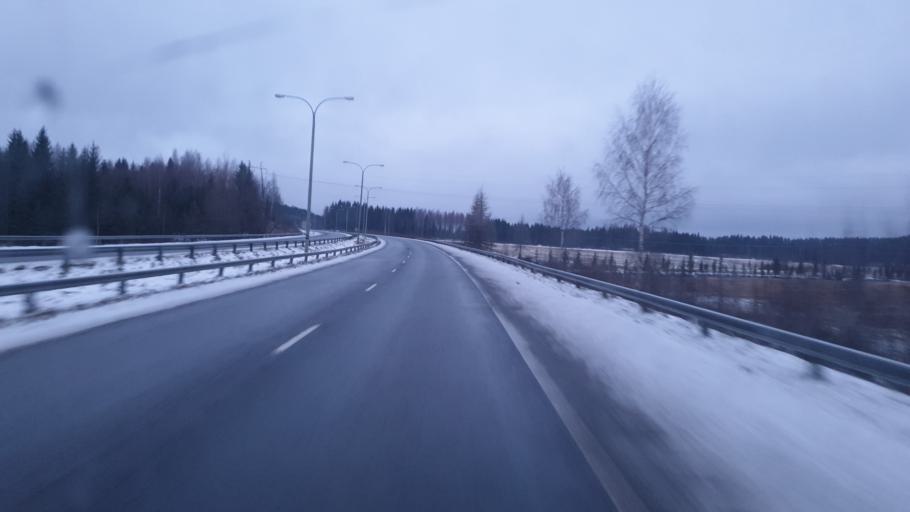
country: FI
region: Northern Savo
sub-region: Kuopio
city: Siilinjaervi
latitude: 63.0490
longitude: 27.6649
